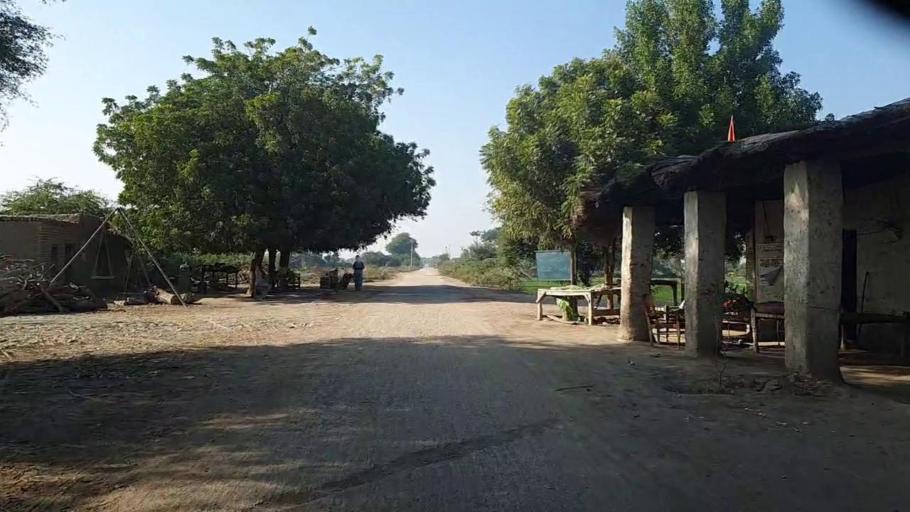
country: PK
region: Sindh
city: Darya Khan Marri
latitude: 26.6747
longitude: 68.3788
